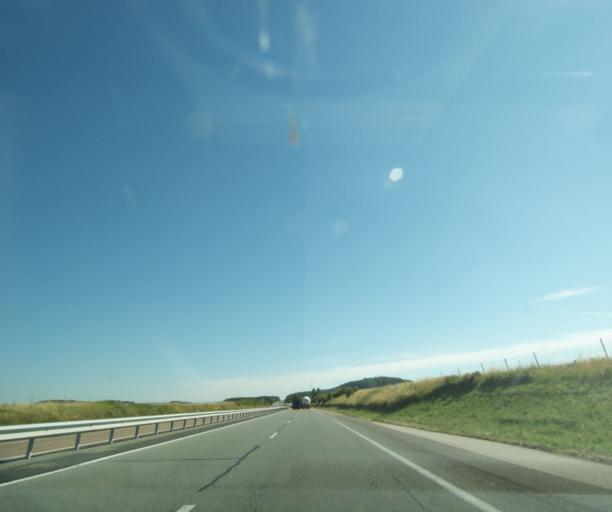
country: FR
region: Champagne-Ardenne
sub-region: Departement de la Haute-Marne
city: Avrecourt
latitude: 48.0494
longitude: 5.5753
